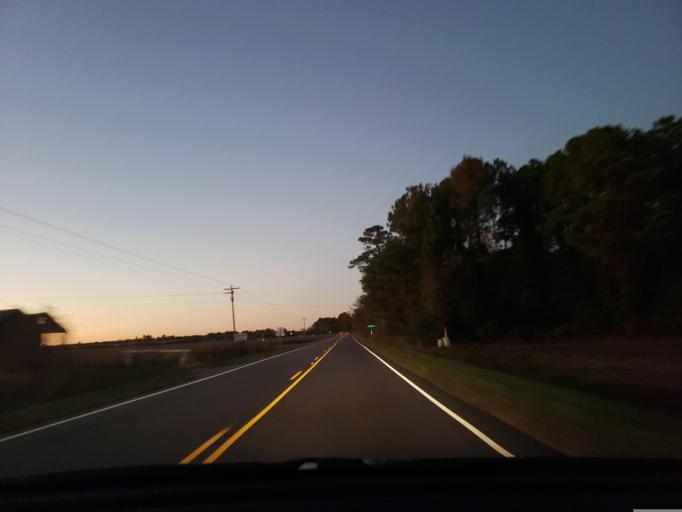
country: US
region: North Carolina
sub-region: Duplin County
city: Kenansville
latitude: 34.9149
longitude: -77.9307
